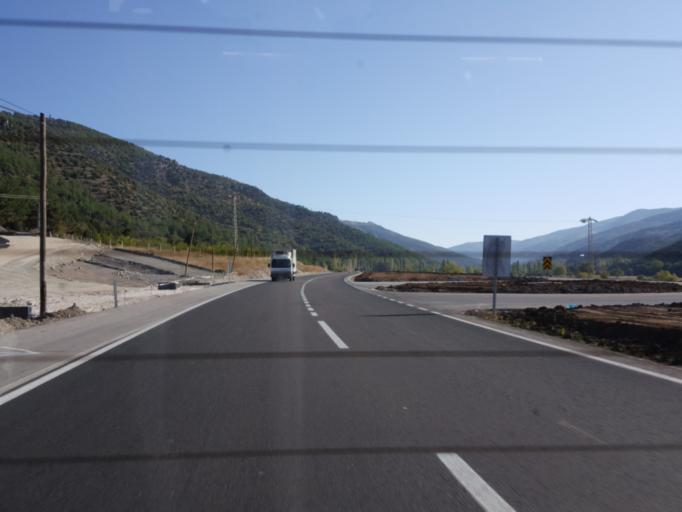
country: TR
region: Tokat
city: Turhal
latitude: 40.4703
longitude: 36.1277
